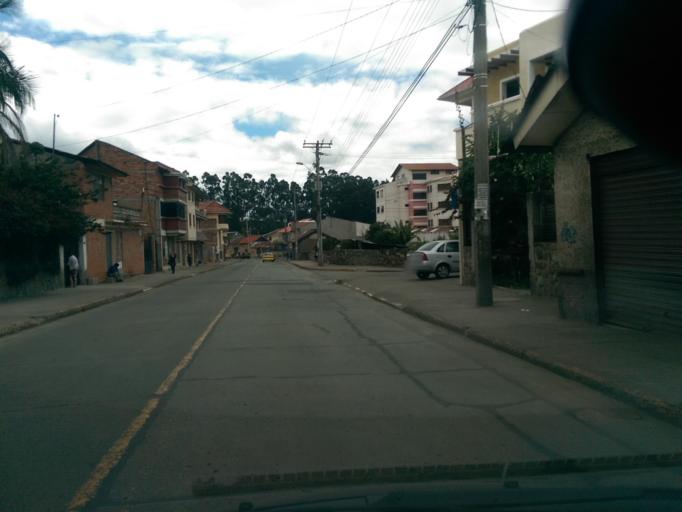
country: EC
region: Azuay
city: Cuenca
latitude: -2.9092
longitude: -79.0277
